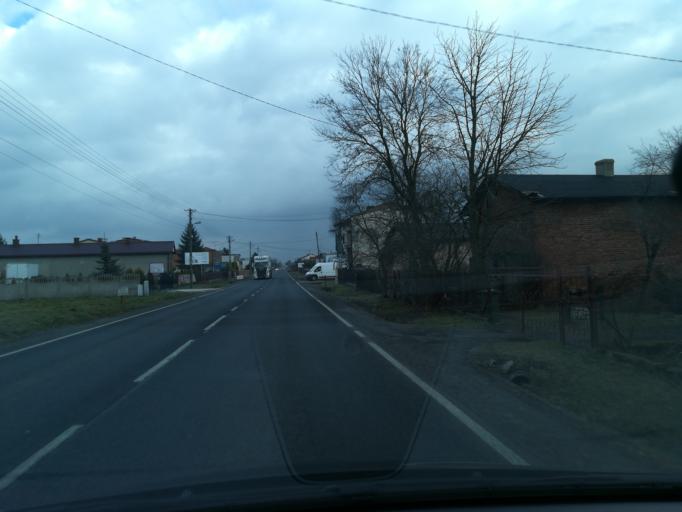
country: PL
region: Lodz Voivodeship
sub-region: Powiat radomszczanski
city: Radomsko
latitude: 51.0788
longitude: 19.3812
